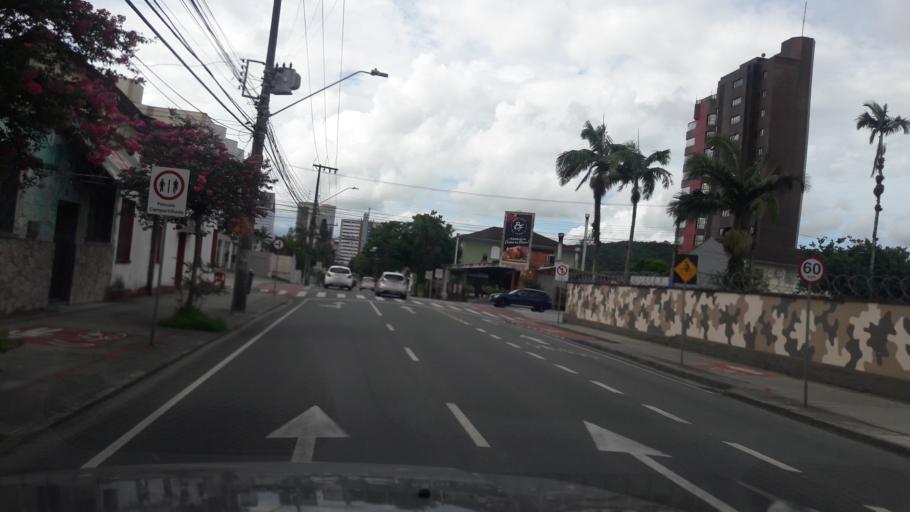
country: BR
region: Santa Catarina
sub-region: Joinville
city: Joinville
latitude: -26.3125
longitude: -48.8428
